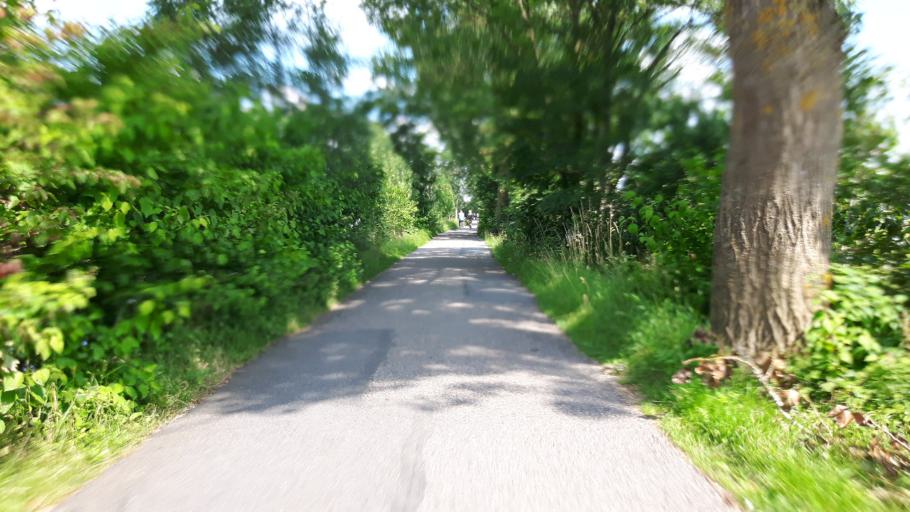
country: NL
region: Utrecht
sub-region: Gemeente Woerden
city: Woerden
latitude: 52.0736
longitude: 4.8870
